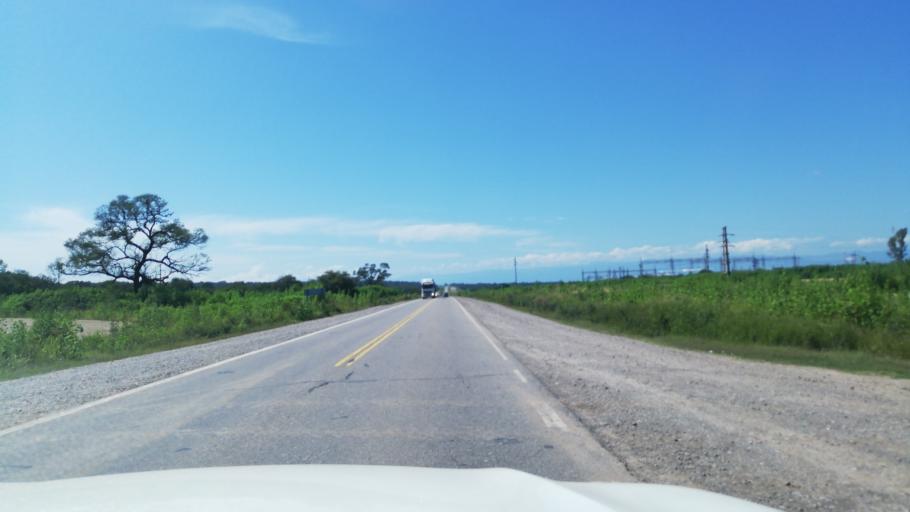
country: AR
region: Jujuy
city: La Mendieta
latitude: -24.3750
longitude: -65.0035
